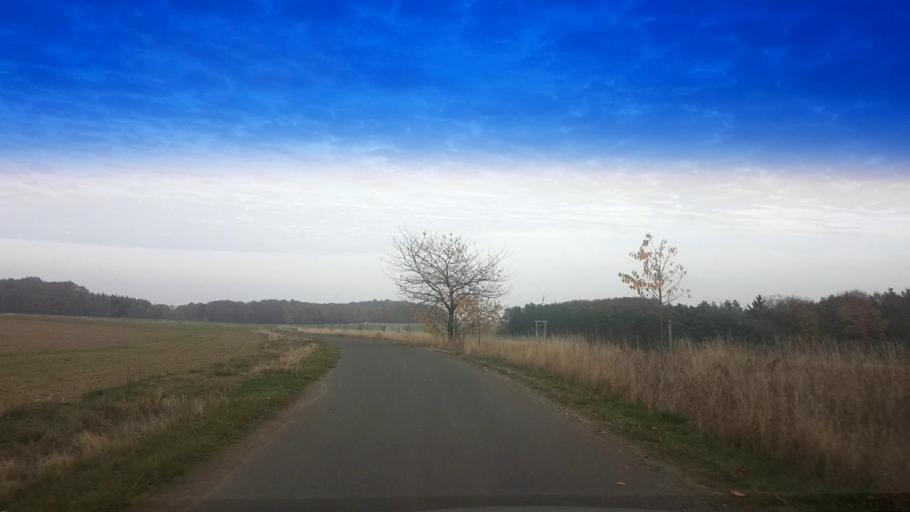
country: DE
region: Bavaria
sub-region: Upper Franconia
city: Priesendorf
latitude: 49.9051
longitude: 10.7372
